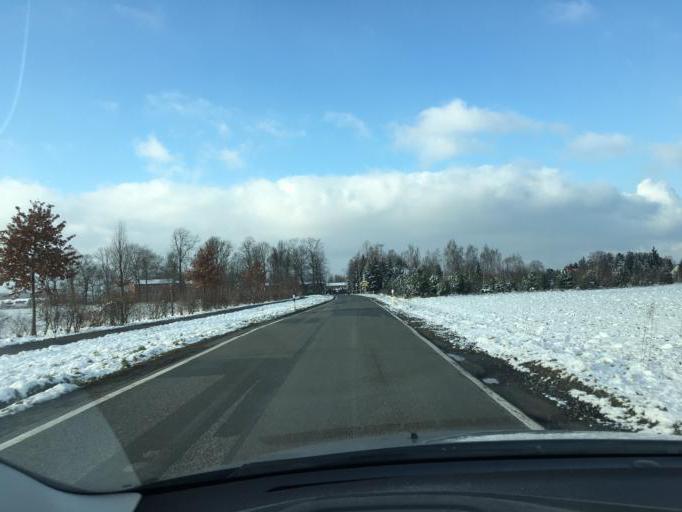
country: DE
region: Saxony
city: Grimma
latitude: 51.2546
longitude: 12.6957
